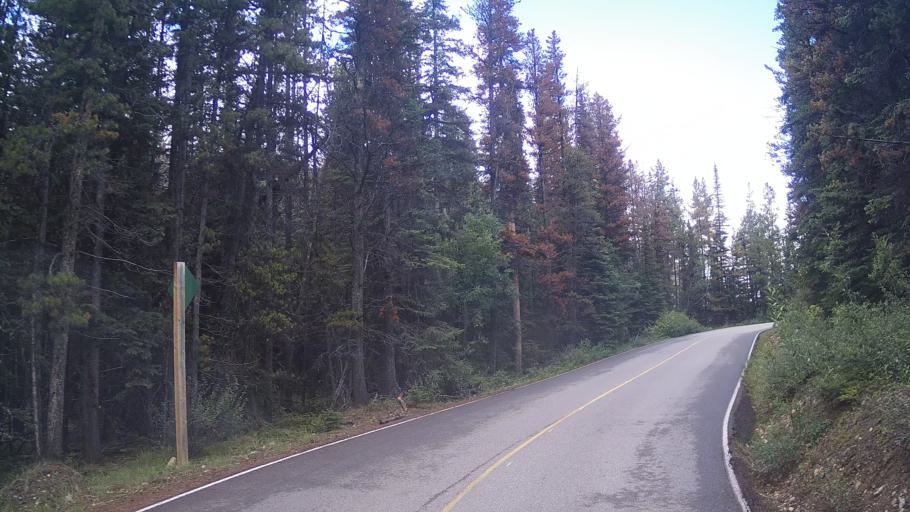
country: CA
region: Alberta
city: Jasper Park Lodge
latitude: 52.7293
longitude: -118.0503
